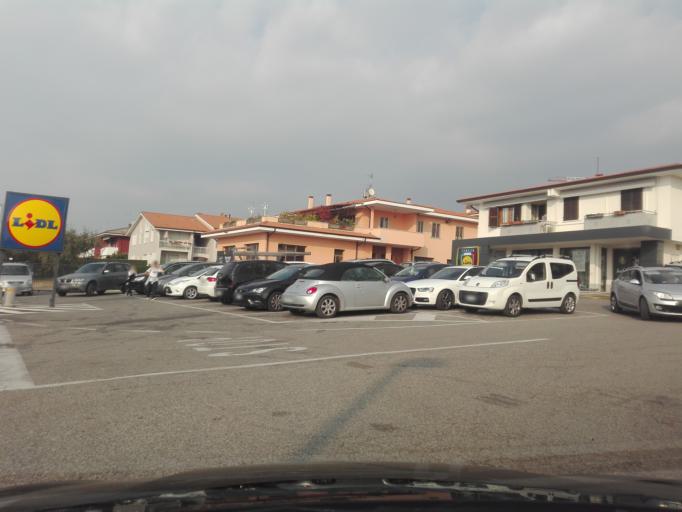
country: IT
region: Veneto
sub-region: Provincia di Verona
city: Bardolino
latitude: 45.5374
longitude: 10.7274
